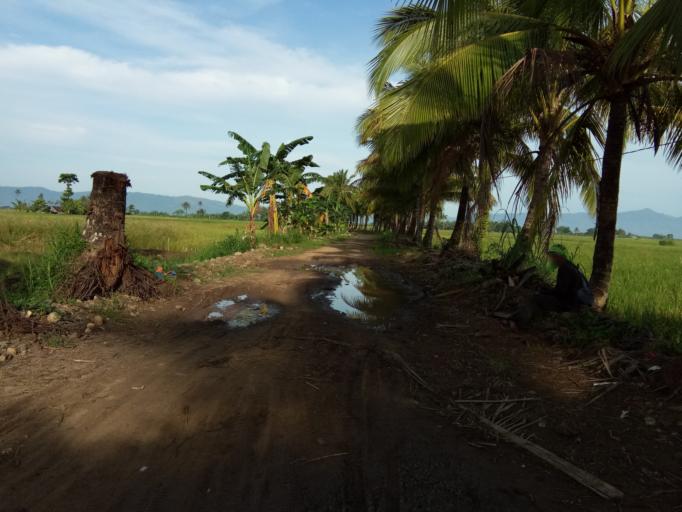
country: PH
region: Caraga
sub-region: Province of Surigao del Norte
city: Alegria
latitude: 9.4961
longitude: 125.5766
